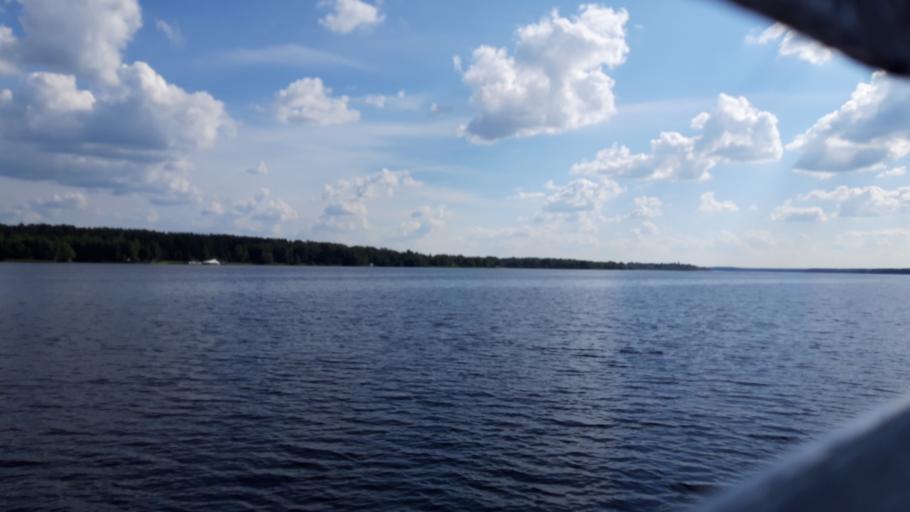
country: RU
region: Tverskaya
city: Konakovo
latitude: 56.6598
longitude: 36.6432
